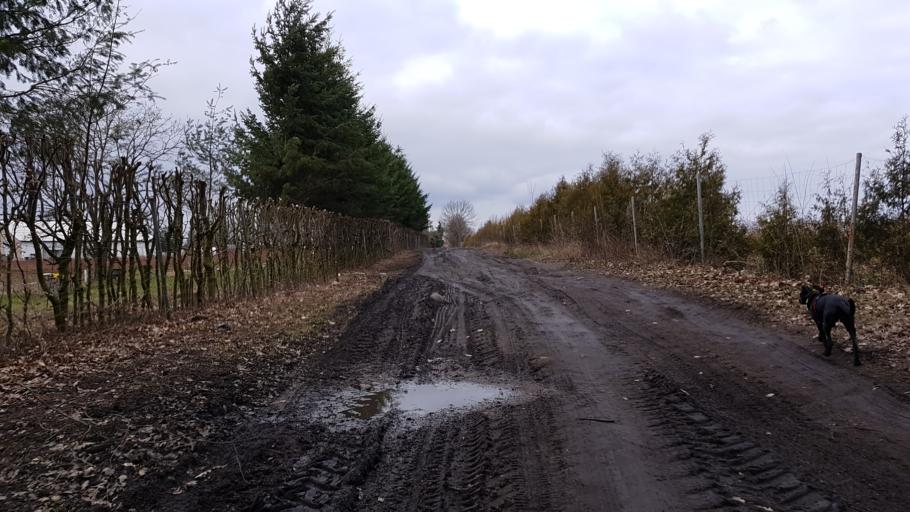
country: PL
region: West Pomeranian Voivodeship
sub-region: Powiat gryfinski
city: Banie
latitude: 53.0927
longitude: 14.7106
